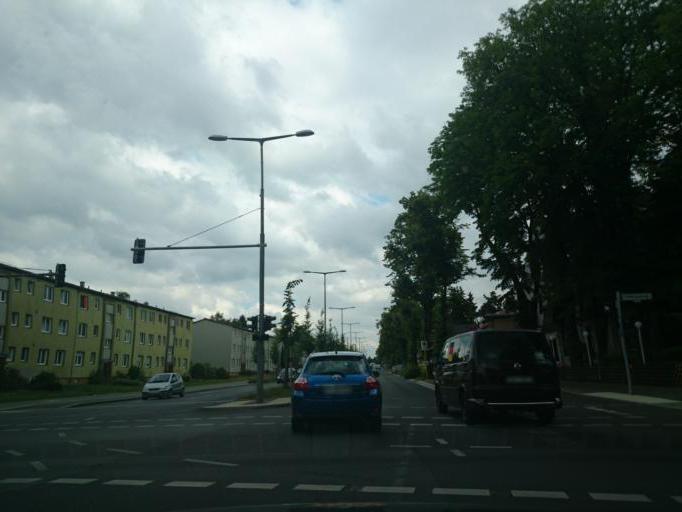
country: DE
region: Berlin
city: Lichtenrade
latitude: 52.3827
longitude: 13.4133
